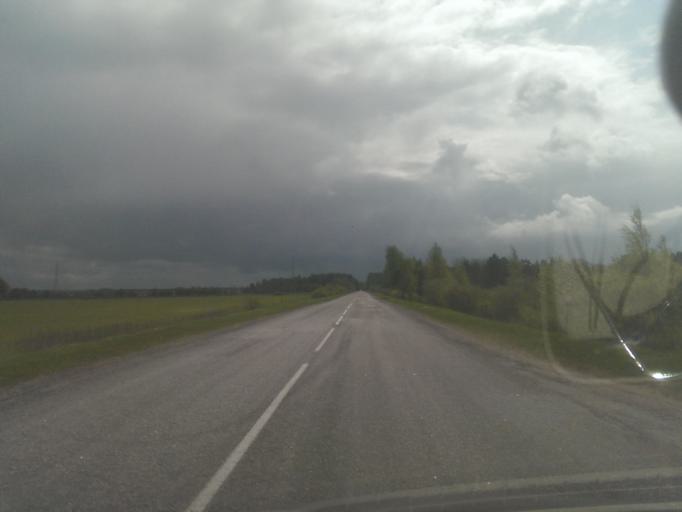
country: LV
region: Ventspils Rajons
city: Piltene
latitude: 57.1905
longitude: 21.6383
